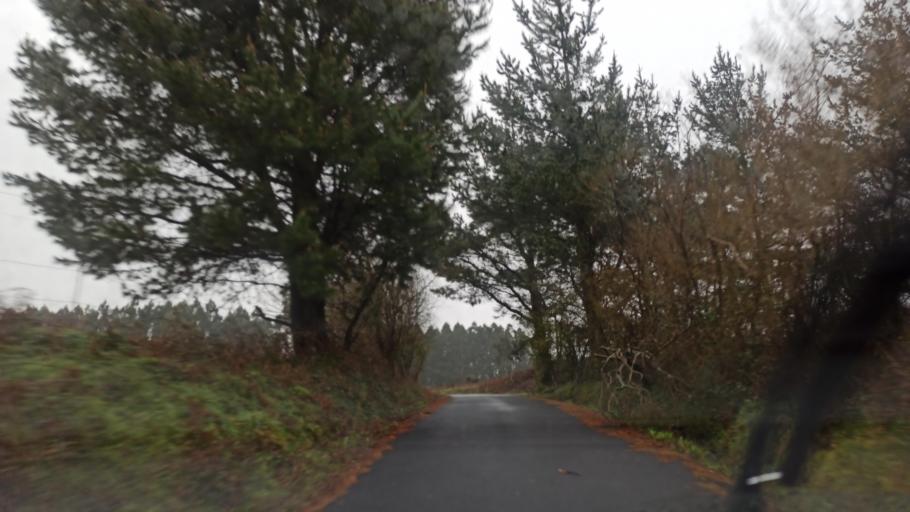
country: ES
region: Galicia
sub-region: Provincia da Coruna
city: Coiros
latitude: 43.1847
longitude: -8.1293
